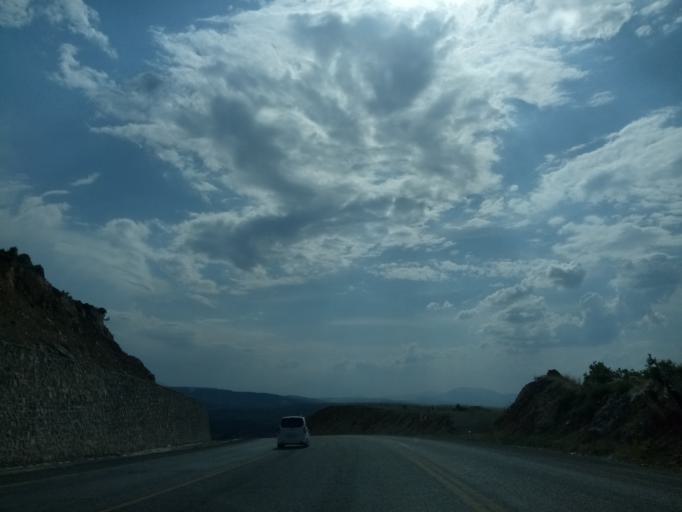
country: TR
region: Isparta
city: Bagkonak
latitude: 38.2256
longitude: 31.2977
